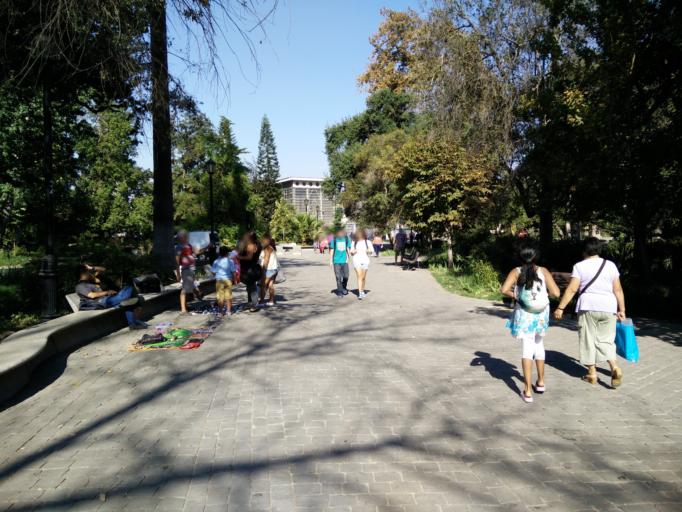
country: CL
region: Santiago Metropolitan
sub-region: Provincia de Santiago
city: Santiago
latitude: -33.4401
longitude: -70.6816
